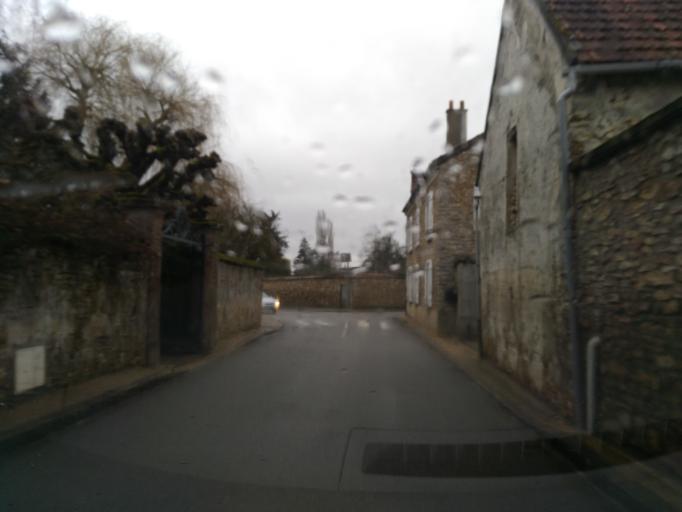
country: FR
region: Ile-de-France
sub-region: Departement des Yvelines
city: Thoiry
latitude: 48.8616
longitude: 1.8153
